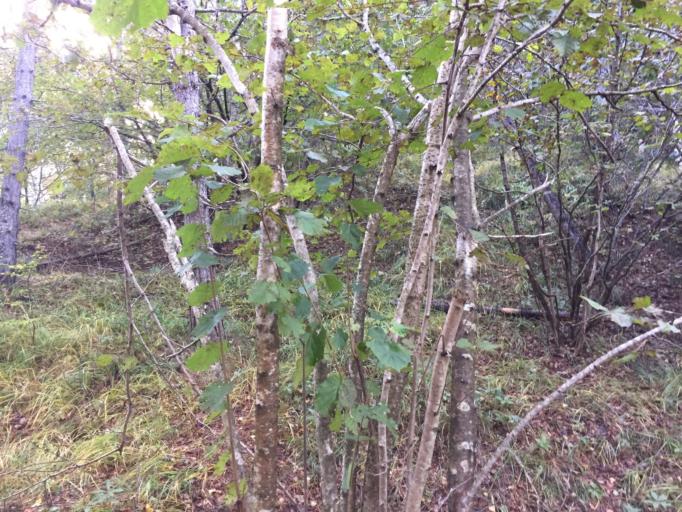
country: IT
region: Friuli Venezia Giulia
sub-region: Provincia di Udine
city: Chiusaforte
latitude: 46.4050
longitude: 13.3349
